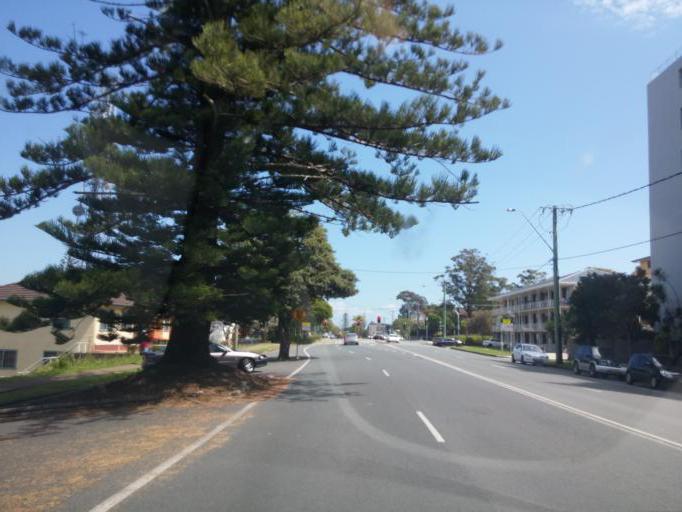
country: AU
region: New South Wales
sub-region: Port Macquarie-Hastings
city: Port Macquarie
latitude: -31.4309
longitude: 152.9161
